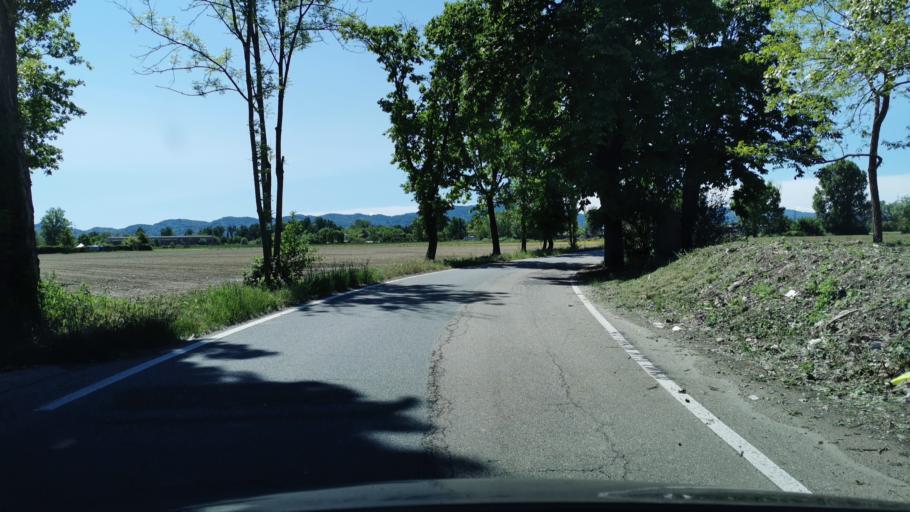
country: IT
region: Piedmont
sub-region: Provincia di Torino
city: Settimo Torinese
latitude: 45.1645
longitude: 7.7441
